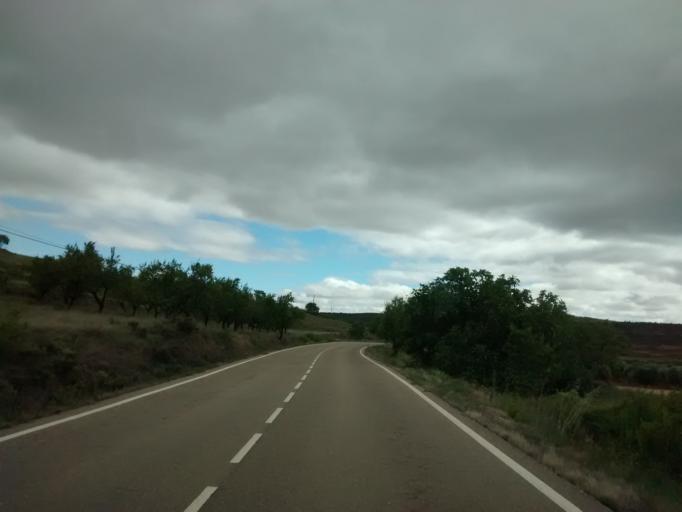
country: ES
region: Aragon
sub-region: Provincia de Zaragoza
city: Trasmoz
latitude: 41.8350
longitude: -1.7134
